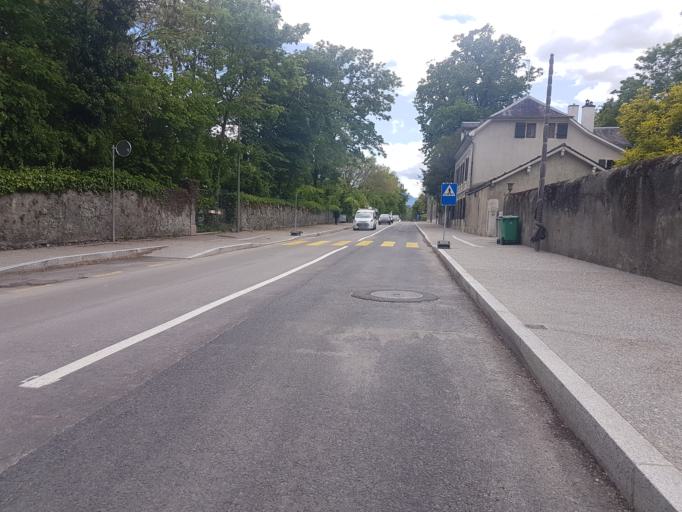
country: CH
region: Geneva
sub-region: Geneva
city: Versoix
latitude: 46.2870
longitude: 6.1657
